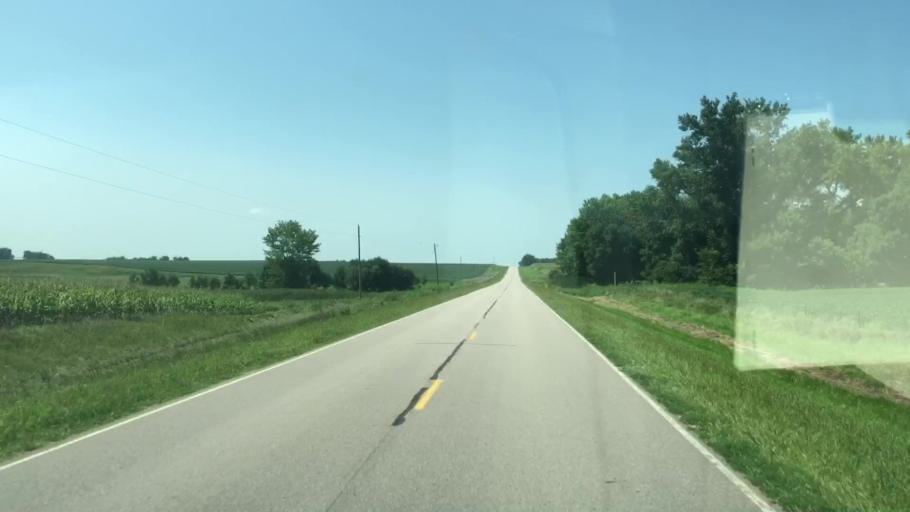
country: US
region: Iowa
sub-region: O'Brien County
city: Sanborn
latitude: 43.2442
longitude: -95.7270
